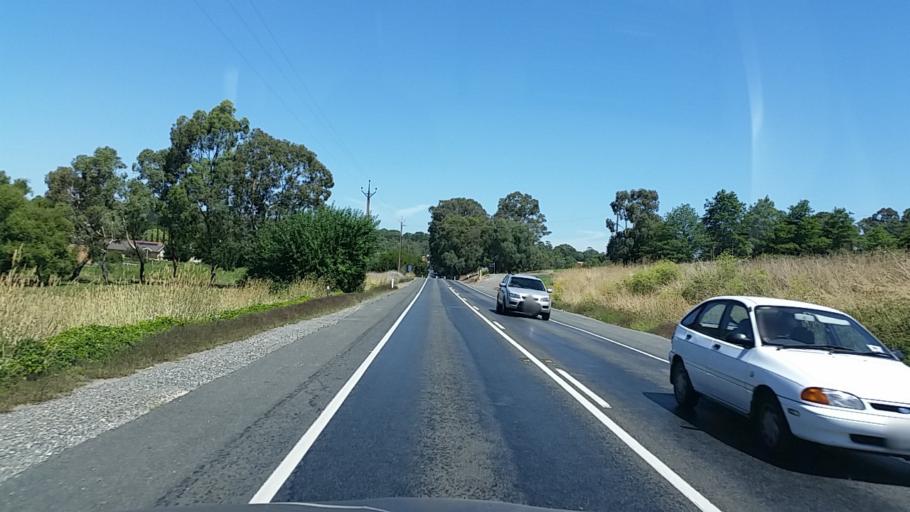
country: AU
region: South Australia
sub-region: Mount Barker
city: Little Hampton
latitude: -35.0416
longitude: 138.8640
